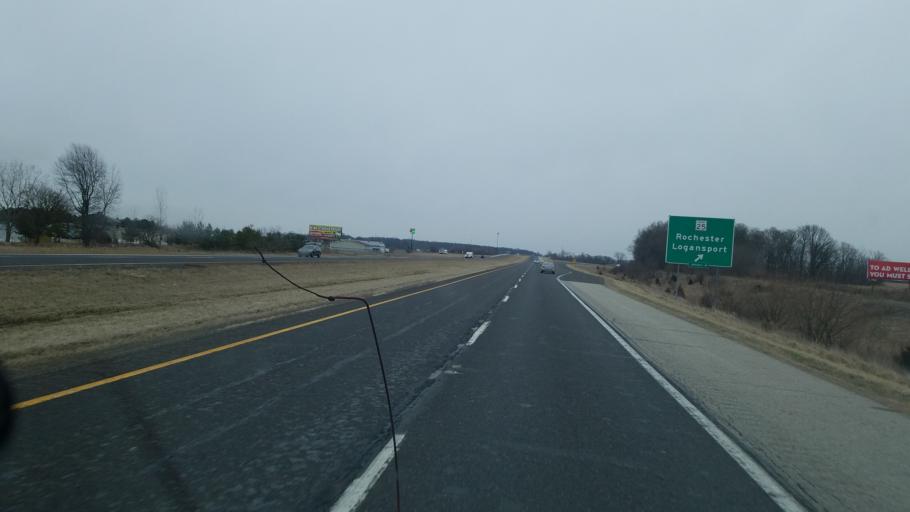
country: US
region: Indiana
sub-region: Fulton County
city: Rochester
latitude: 41.0480
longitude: -86.2291
